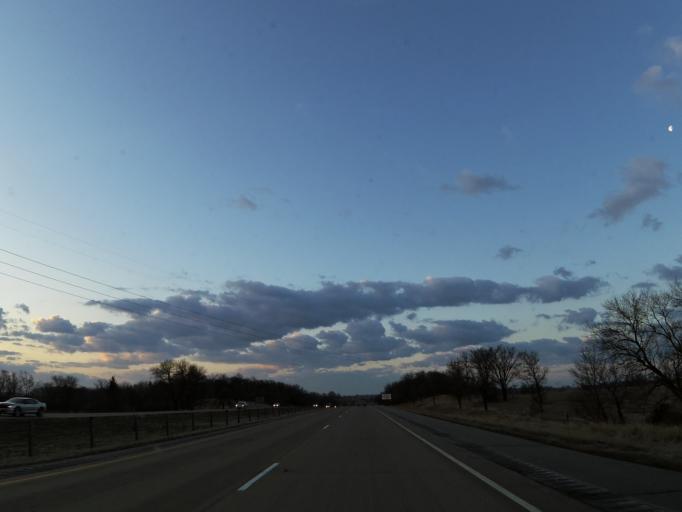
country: US
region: Minnesota
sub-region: Scott County
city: Elko New Market
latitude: 44.5193
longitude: -93.2926
